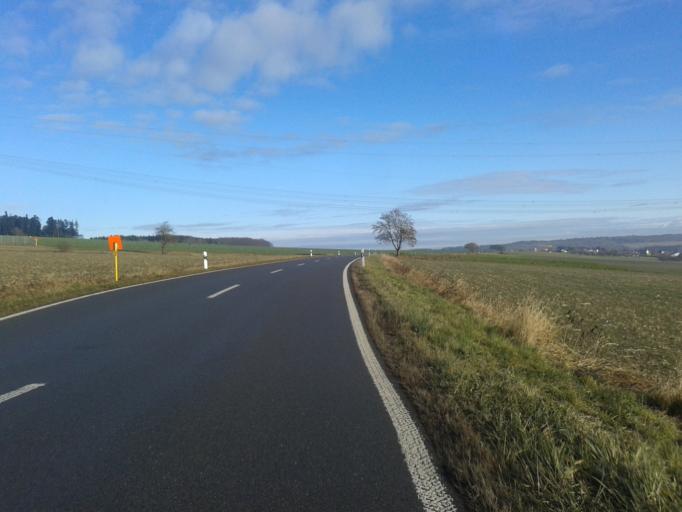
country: DE
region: Baden-Wuerttemberg
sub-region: Tuebingen Region
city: Blaubeuren
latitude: 48.3871
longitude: 9.8430
